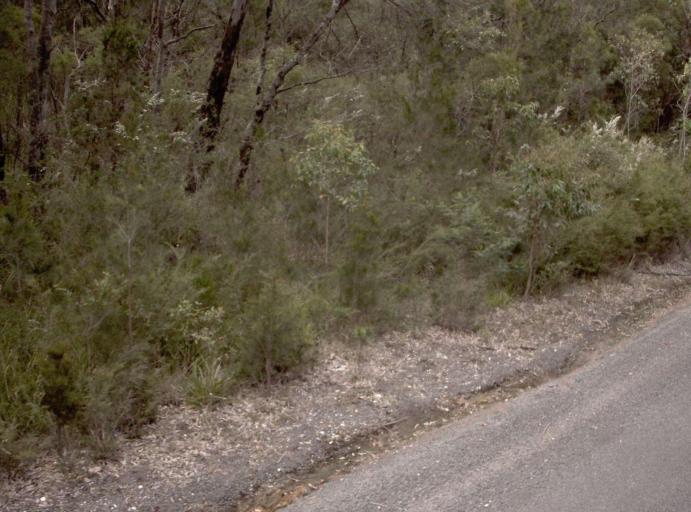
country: AU
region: New South Wales
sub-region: Bega Valley
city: Eden
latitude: -37.4600
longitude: 149.6079
